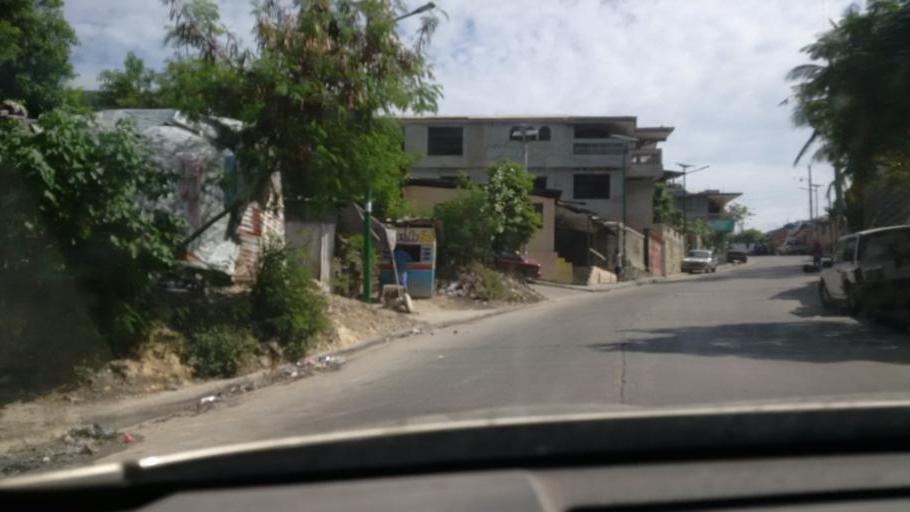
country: HT
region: Ouest
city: Delmas 73
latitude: 18.5401
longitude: -72.3127
